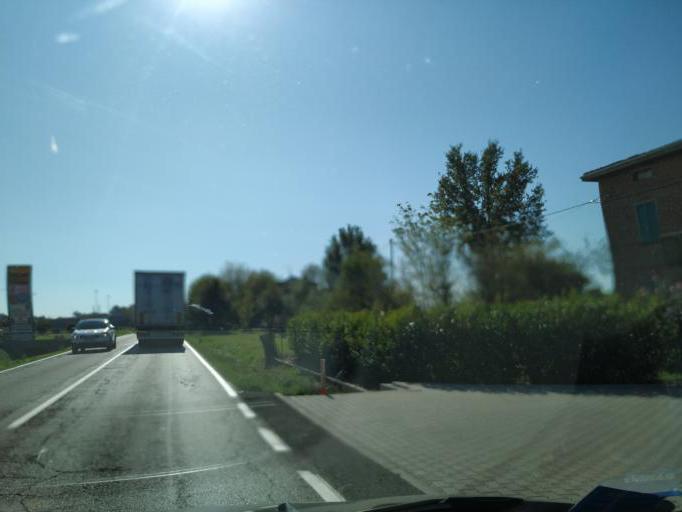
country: IT
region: Emilia-Romagna
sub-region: Provincia di Bologna
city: Sant'Agata Bolognese
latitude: 44.6563
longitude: 11.1367
